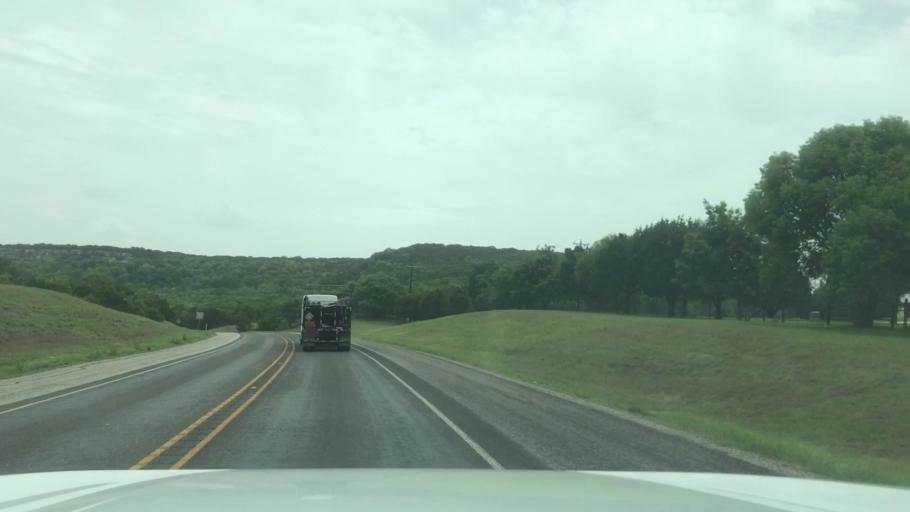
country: US
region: Texas
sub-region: Bosque County
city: Meridian
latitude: 31.9043
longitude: -97.6605
